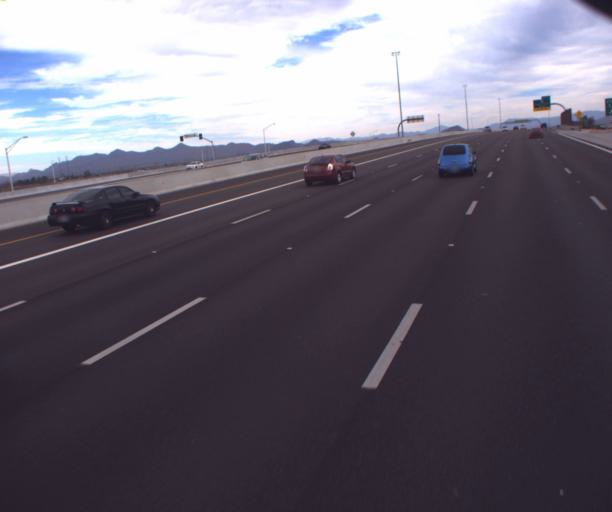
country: US
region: Arizona
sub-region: Maricopa County
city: Mesa
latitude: 33.4494
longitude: -111.8505
